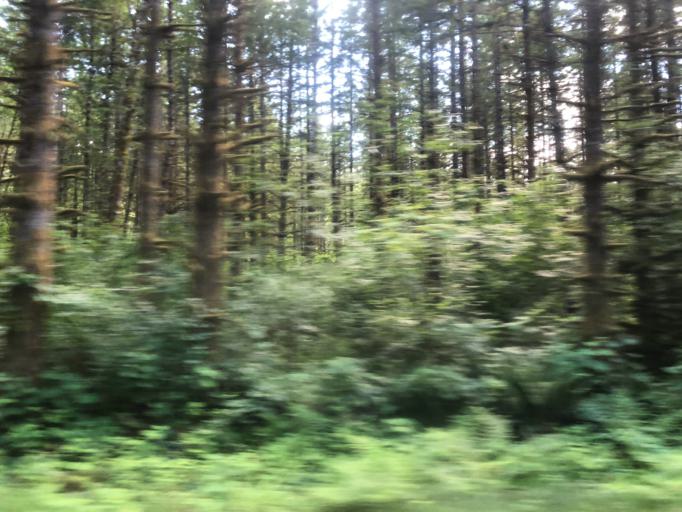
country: US
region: Oregon
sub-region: Clackamas County
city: Sandy
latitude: 45.4285
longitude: -122.2300
